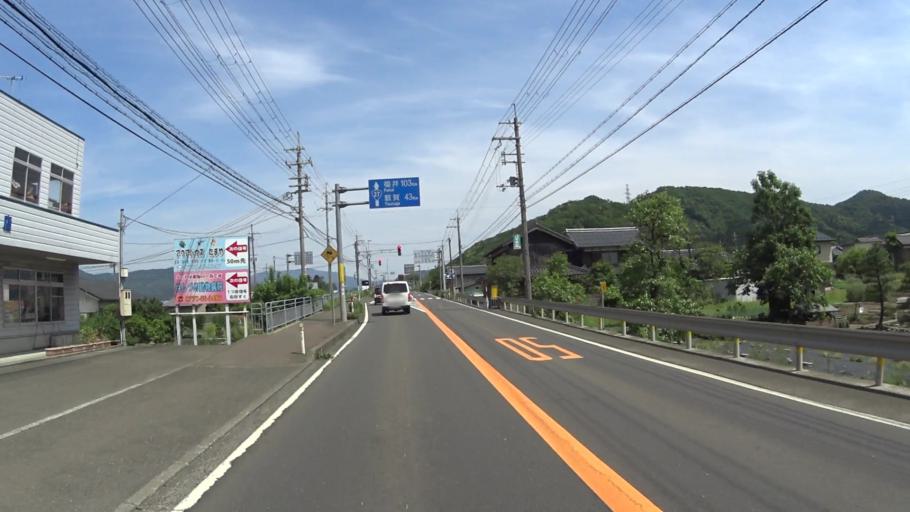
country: JP
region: Fukui
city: Obama
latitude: 35.4819
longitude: 135.7825
